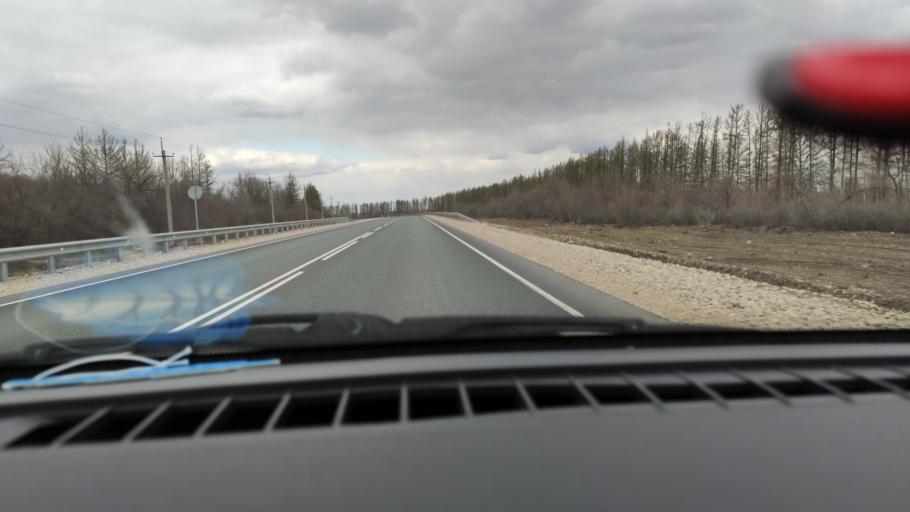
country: RU
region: Saratov
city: Shikhany
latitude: 52.1615
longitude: 47.1651
